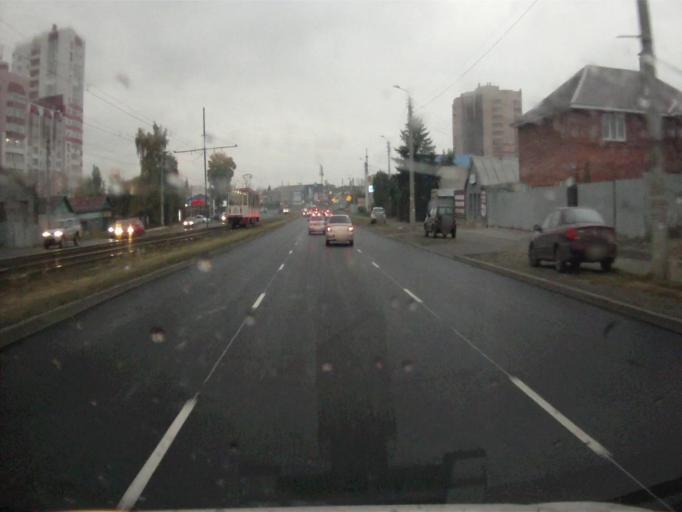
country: RU
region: Chelyabinsk
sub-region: Gorod Chelyabinsk
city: Chelyabinsk
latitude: 55.1838
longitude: 61.3765
